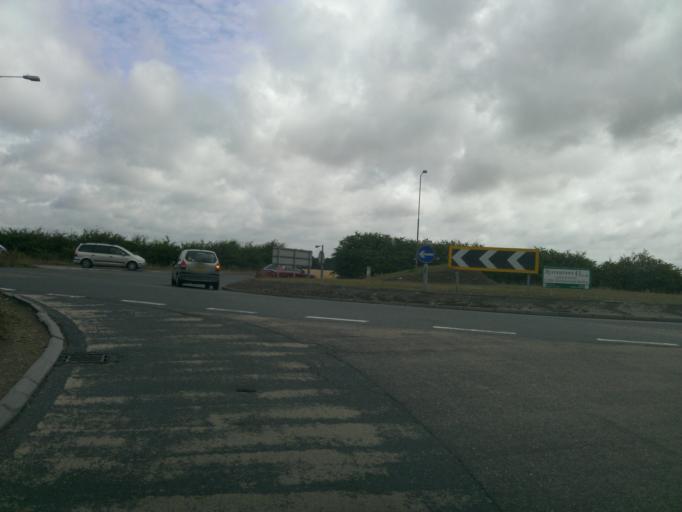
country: GB
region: England
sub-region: Essex
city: Great Bentley
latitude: 51.8713
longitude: 1.0550
